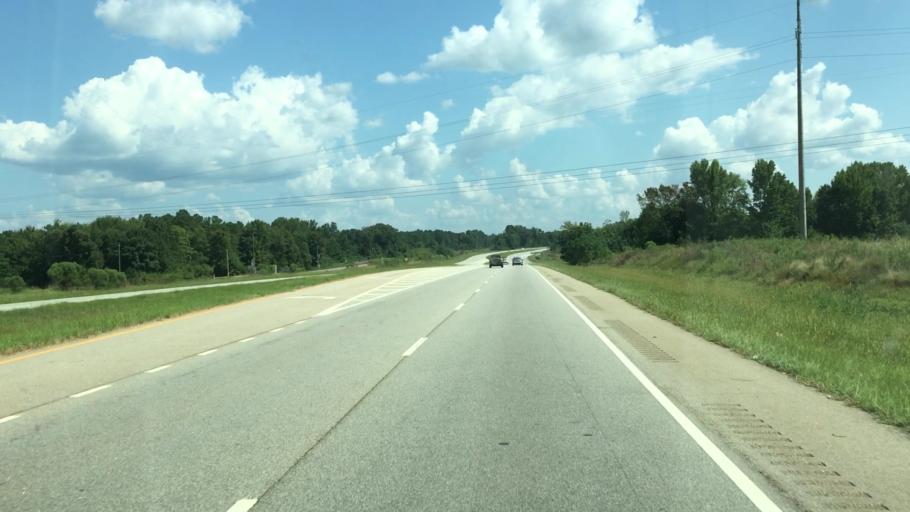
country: US
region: Georgia
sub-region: Putnam County
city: Eatonton
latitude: 33.2933
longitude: -83.3771
